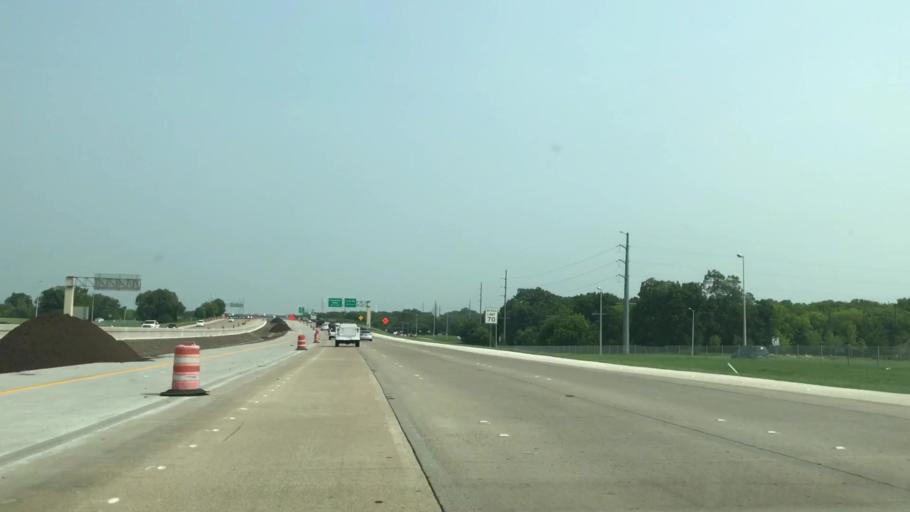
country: US
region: Texas
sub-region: Dallas County
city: Sachse
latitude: 32.9601
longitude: -96.6347
